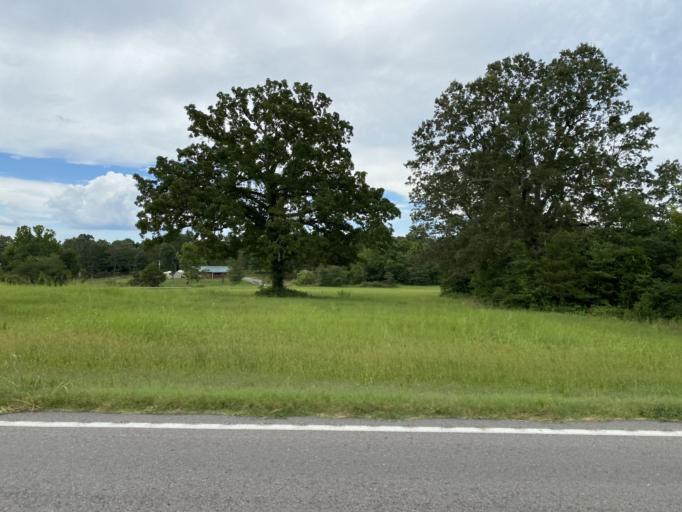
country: US
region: Arkansas
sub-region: Fulton County
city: Salem
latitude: 36.3598
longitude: -91.8338
